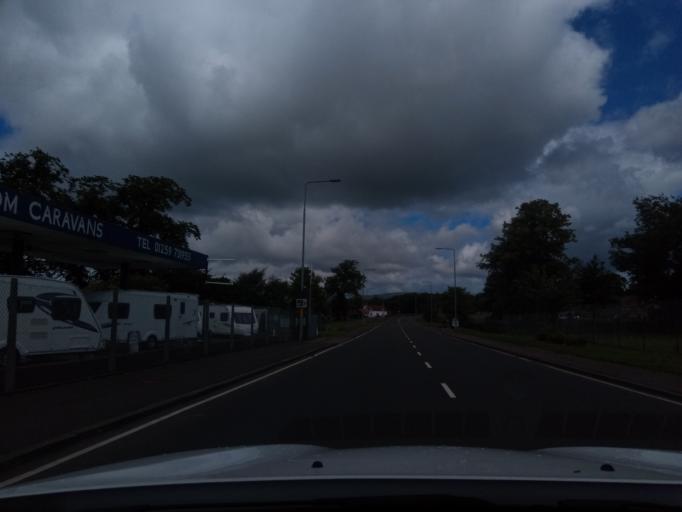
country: GB
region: Scotland
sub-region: Fife
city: Kincardine
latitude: 56.0723
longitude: -3.7199
